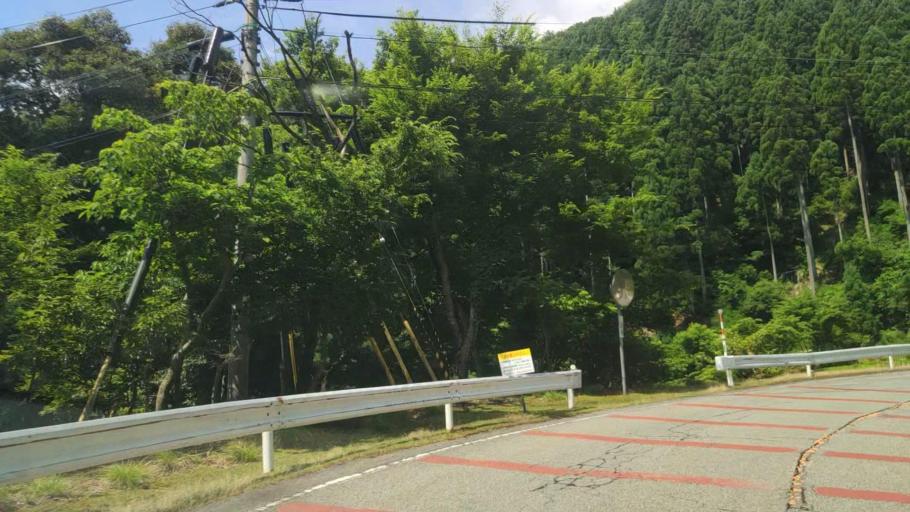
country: JP
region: Hyogo
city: Toyooka
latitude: 35.6367
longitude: 134.7795
